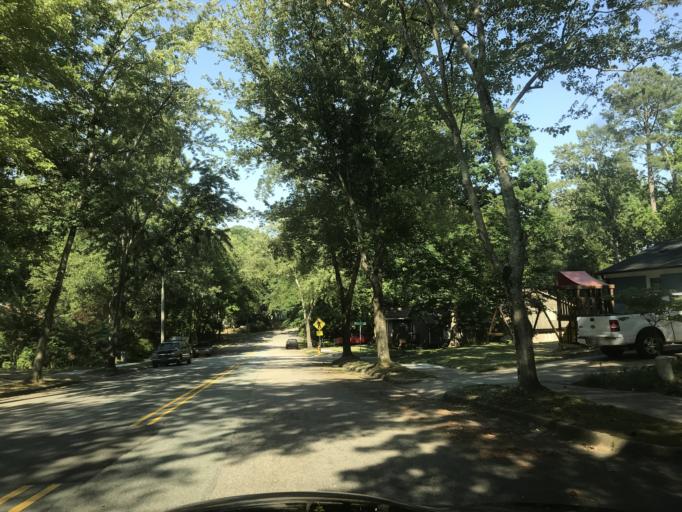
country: US
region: North Carolina
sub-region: Wake County
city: West Raleigh
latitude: 35.8633
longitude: -78.6131
